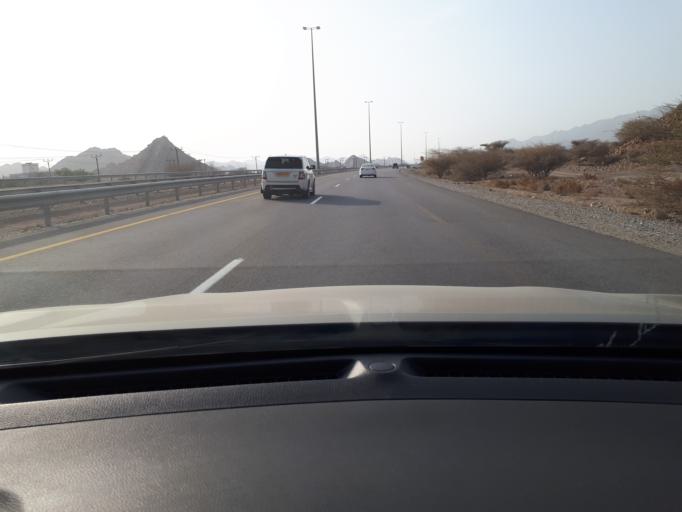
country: OM
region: Muhafazat Masqat
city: Muscat
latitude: 23.2781
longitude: 58.7527
